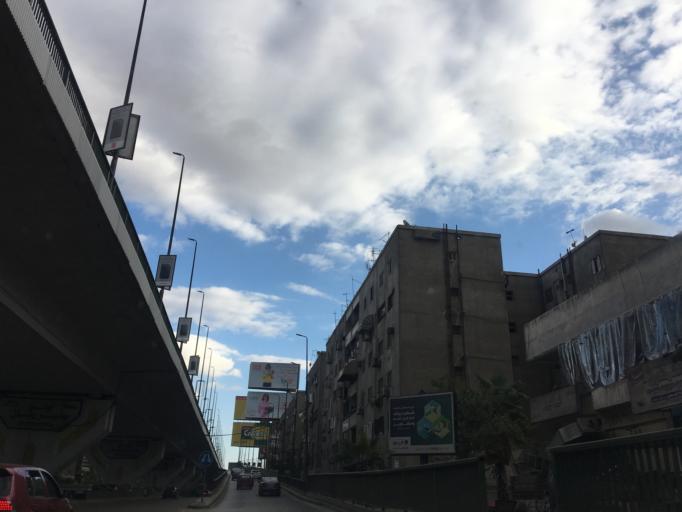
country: EG
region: Muhafazat al Qahirah
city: Cairo
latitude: 30.0641
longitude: 31.2973
